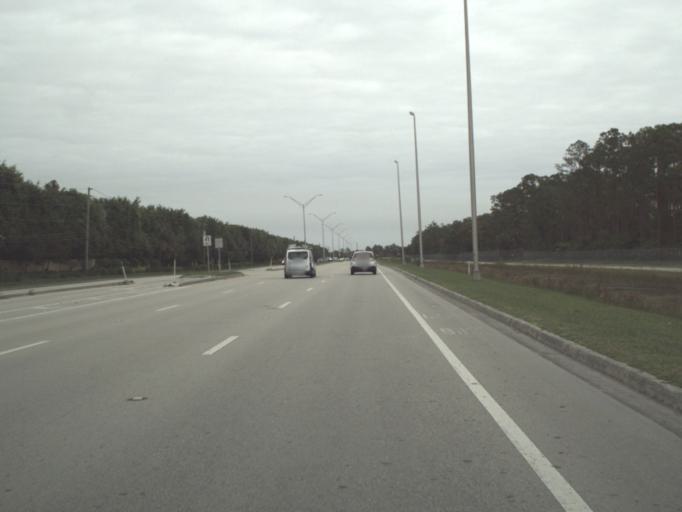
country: US
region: Florida
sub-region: Collier County
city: Lely Resort
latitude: 26.0702
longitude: -81.6938
